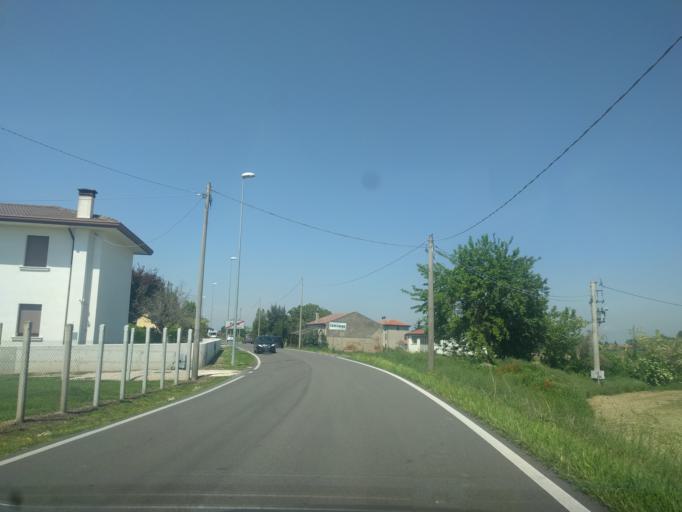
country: IT
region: Veneto
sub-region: Provincia di Rovigo
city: Ceregnano
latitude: 45.0423
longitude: 11.8807
